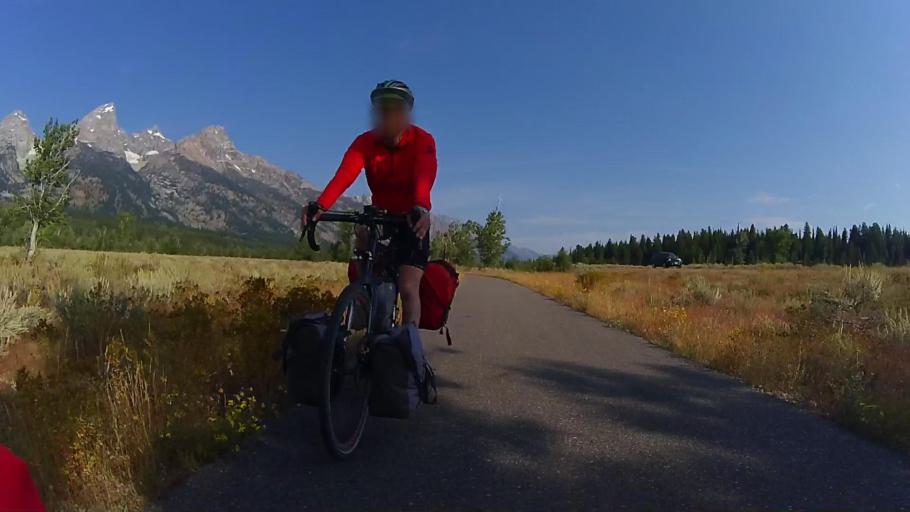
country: US
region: Wyoming
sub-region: Teton County
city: Moose Wilson Road
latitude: 43.7088
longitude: -110.7259
